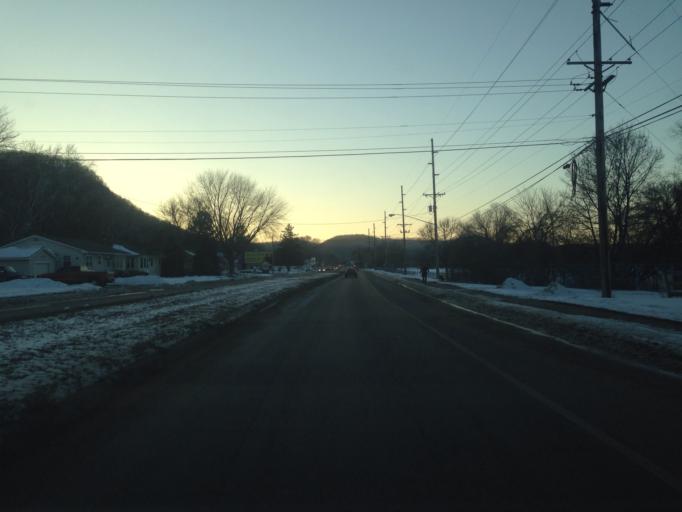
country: US
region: Minnesota
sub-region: Winona County
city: Goodview
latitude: 44.0486
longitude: -91.6698
